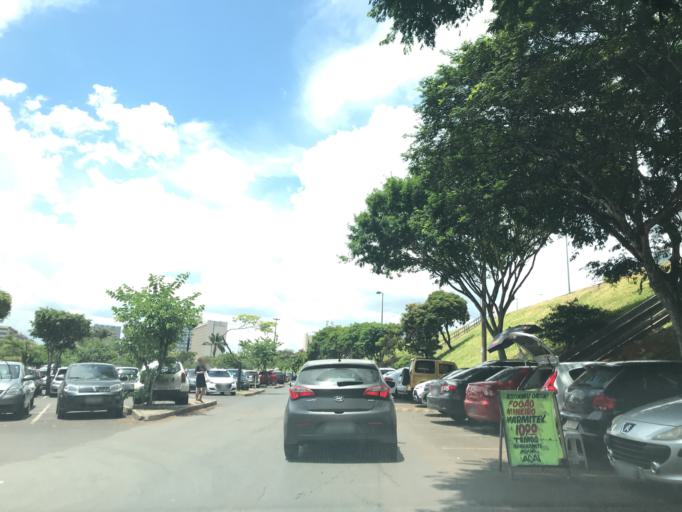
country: BR
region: Federal District
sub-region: Brasilia
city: Brasilia
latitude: -15.7906
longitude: -47.8839
